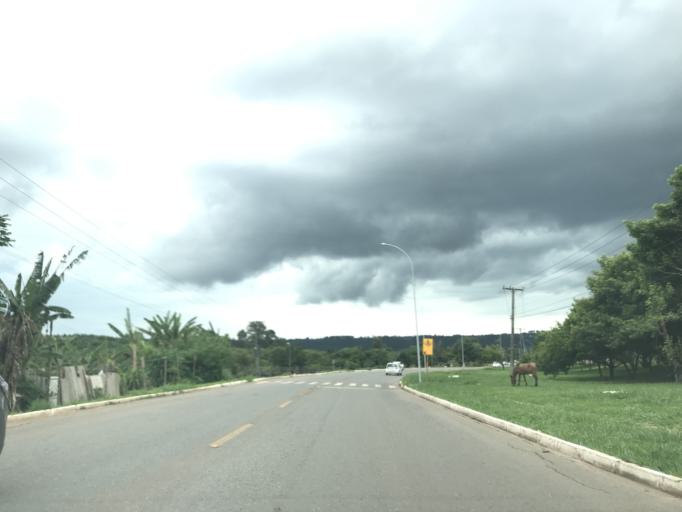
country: BR
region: Federal District
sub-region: Brasilia
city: Brasilia
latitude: -15.6496
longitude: -47.8132
